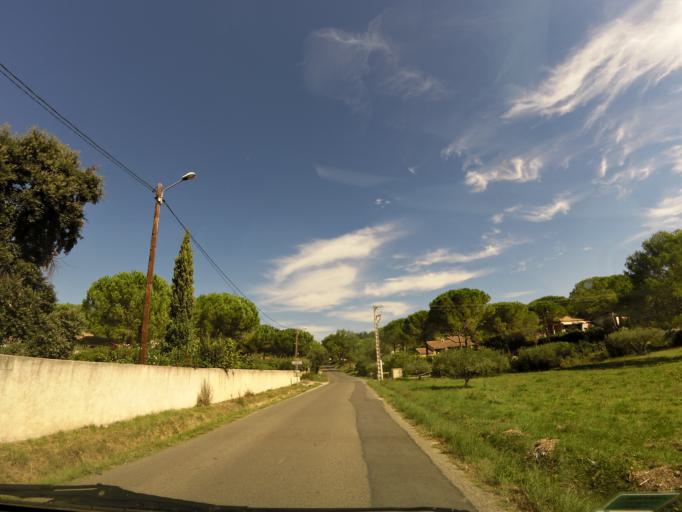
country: FR
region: Languedoc-Roussillon
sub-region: Departement du Gard
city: Langlade
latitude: 43.7938
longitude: 4.2439
